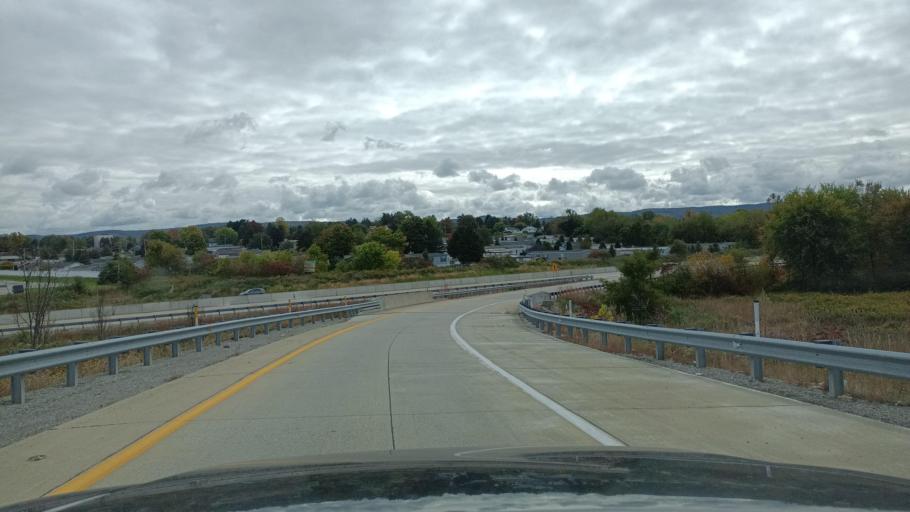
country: US
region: Pennsylvania
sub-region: Westmoreland County
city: Mount Pleasant
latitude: 40.1219
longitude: -79.5568
